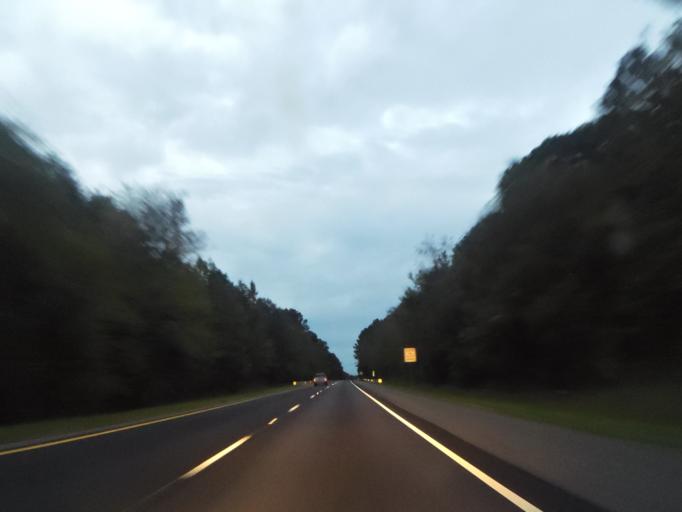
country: US
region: Alabama
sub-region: DeKalb County
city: Crossville
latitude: 34.2026
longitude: -85.9419
